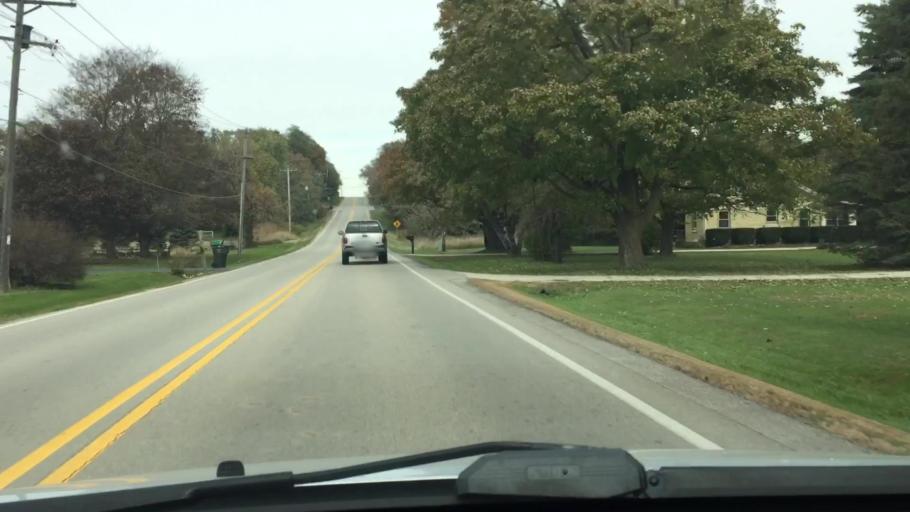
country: US
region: Wisconsin
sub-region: Waukesha County
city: North Prairie
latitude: 42.9203
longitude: -88.4054
